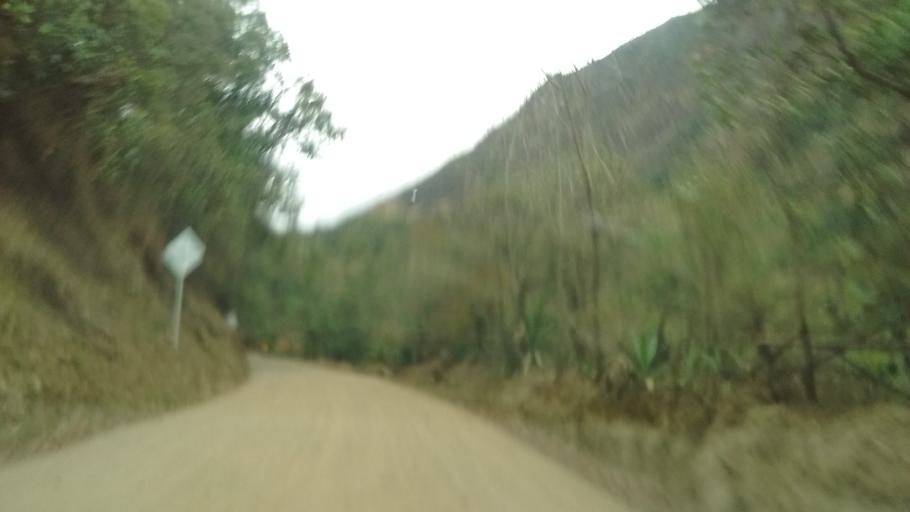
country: CO
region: Cauca
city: La Vega
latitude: 2.0135
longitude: -76.7926
